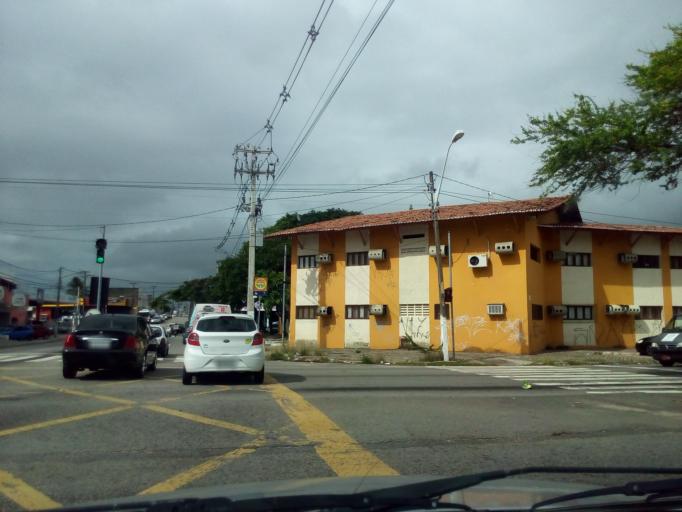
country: BR
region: Rio Grande do Norte
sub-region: Natal
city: Natal
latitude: -5.8105
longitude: -35.2118
